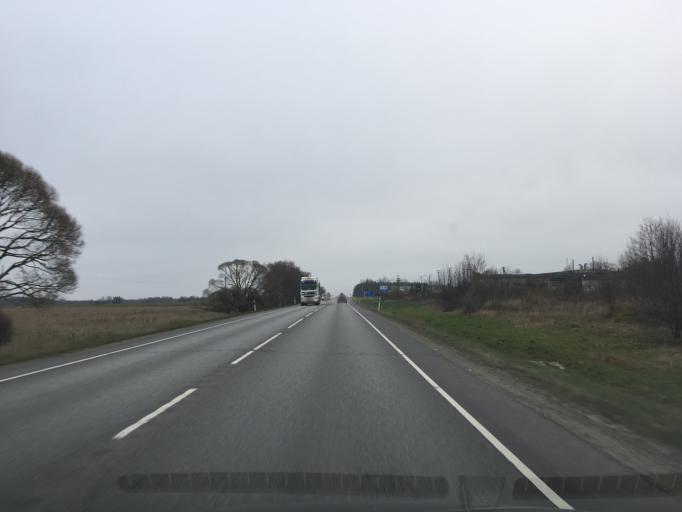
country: EE
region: Ida-Virumaa
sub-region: Kohtla-Jaerve linn
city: Kohtla-Jarve
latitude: 59.4123
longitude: 27.3050
